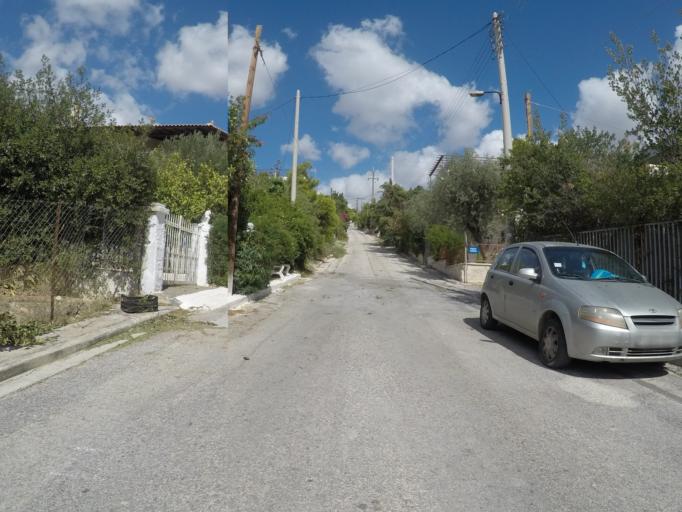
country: GR
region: Attica
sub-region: Nomarchia Anatolikis Attikis
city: Agios Dimitrios Kropias
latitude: 37.7993
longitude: 23.8743
